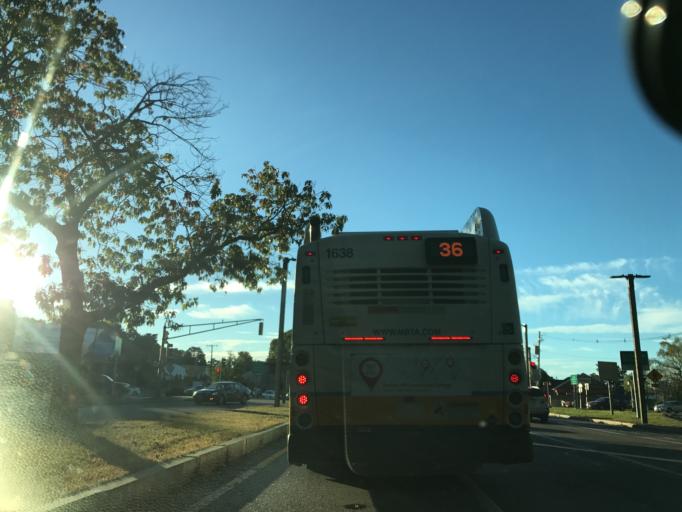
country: US
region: Massachusetts
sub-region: Norfolk County
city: Dedham
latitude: 42.2719
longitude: -71.1731
